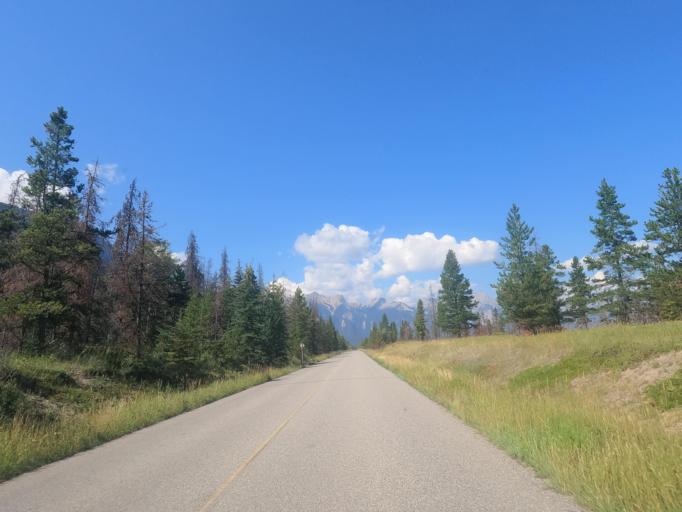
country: CA
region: Alberta
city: Jasper Park Lodge
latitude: 52.9752
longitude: -118.0642
